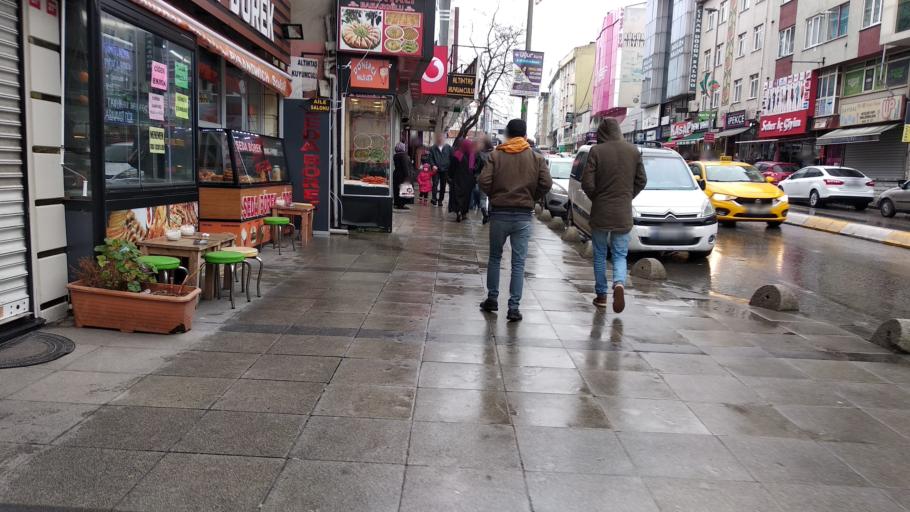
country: TR
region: Istanbul
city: Samandira
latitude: 41.0183
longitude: 29.1920
